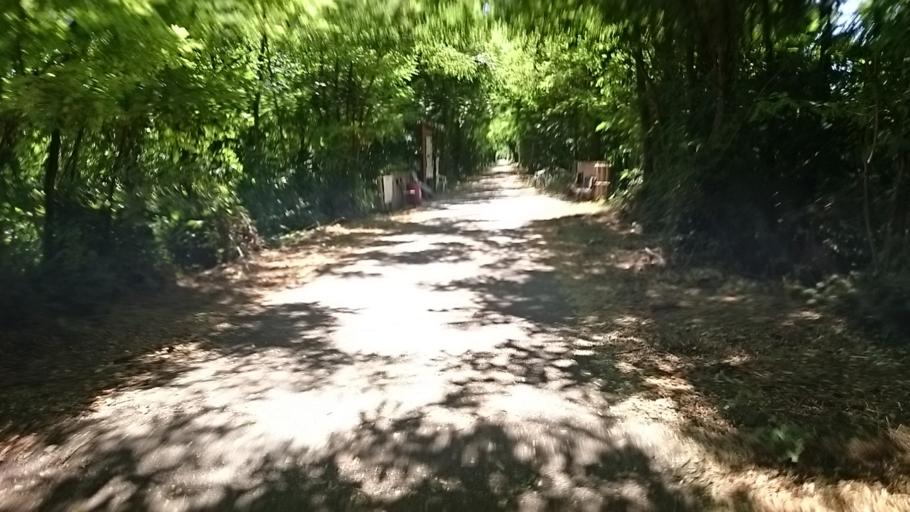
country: IT
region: Veneto
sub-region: Provincia di Padova
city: Piombino Dese
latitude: 45.6058
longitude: 12.0167
